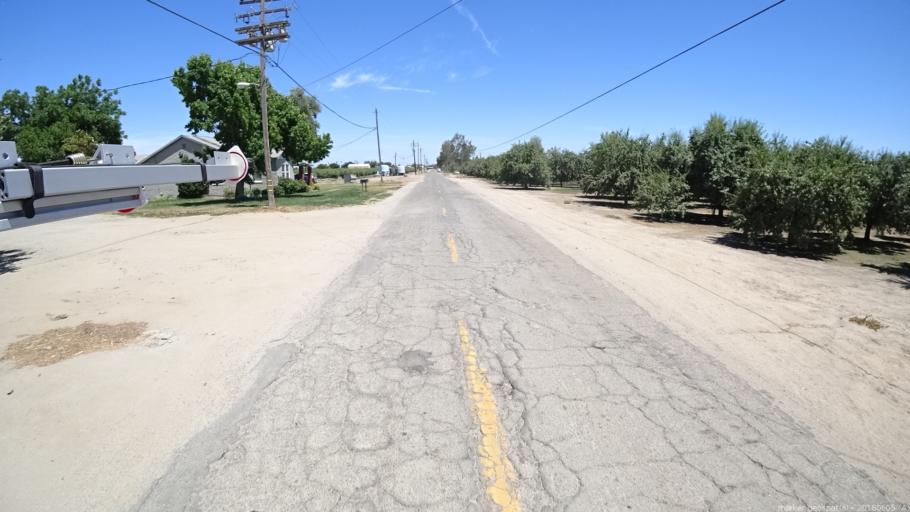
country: US
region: California
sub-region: Madera County
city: Chowchilla
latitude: 37.0907
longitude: -120.2993
